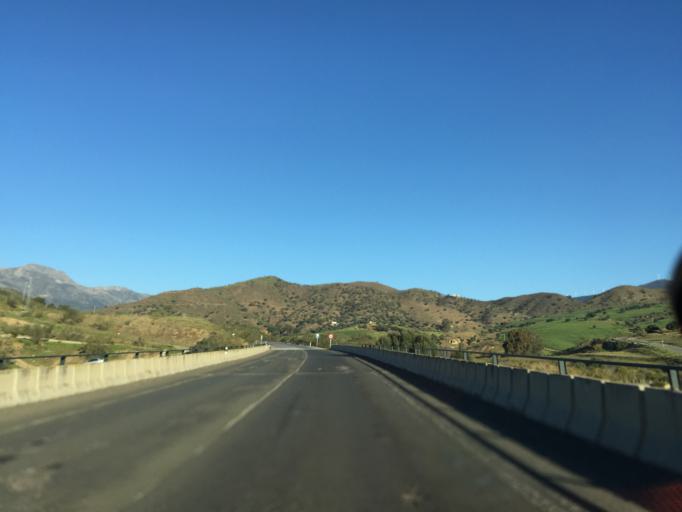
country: ES
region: Andalusia
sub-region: Provincia de Malaga
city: Alora
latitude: 36.8010
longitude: -4.7568
